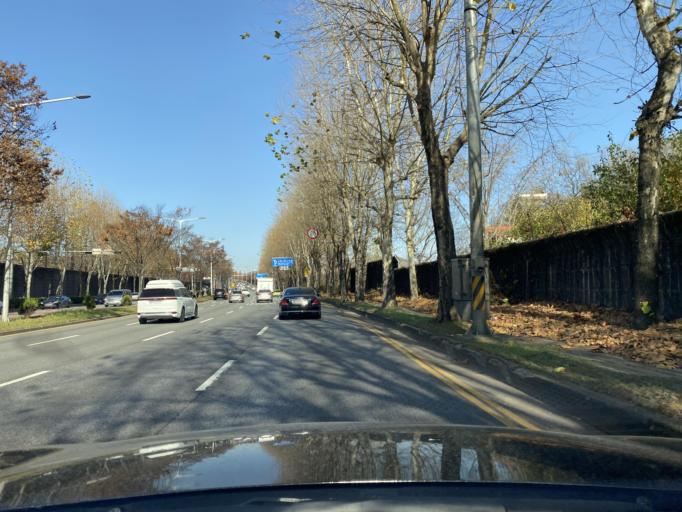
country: KR
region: Incheon
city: Incheon
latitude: 37.4422
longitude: 126.7427
